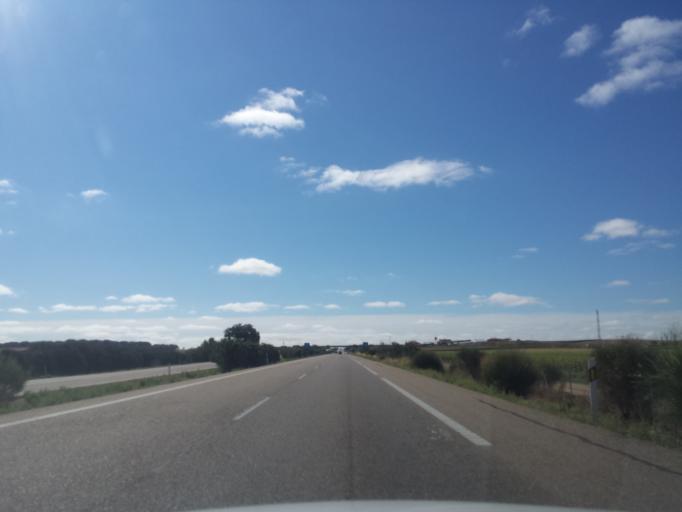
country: ES
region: Castille and Leon
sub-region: Provincia de Zamora
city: Villalpando
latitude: 41.8344
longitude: -5.3858
